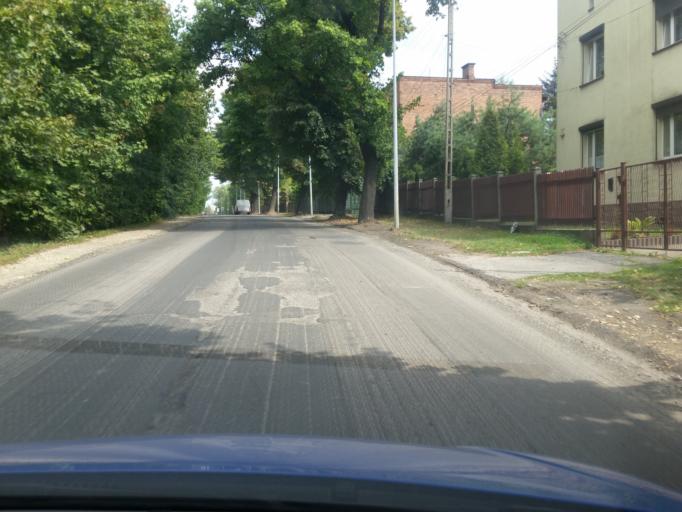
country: PL
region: Silesian Voivodeship
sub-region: Sosnowiec
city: Sosnowiec
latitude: 50.2436
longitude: 19.1038
